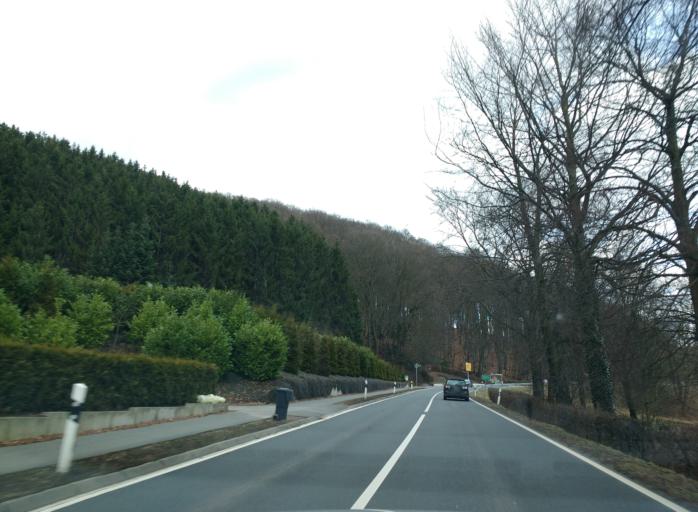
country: DE
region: North Rhine-Westphalia
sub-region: Regierungsbezirk Detmold
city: Lemgo
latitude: 52.0823
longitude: 8.9316
